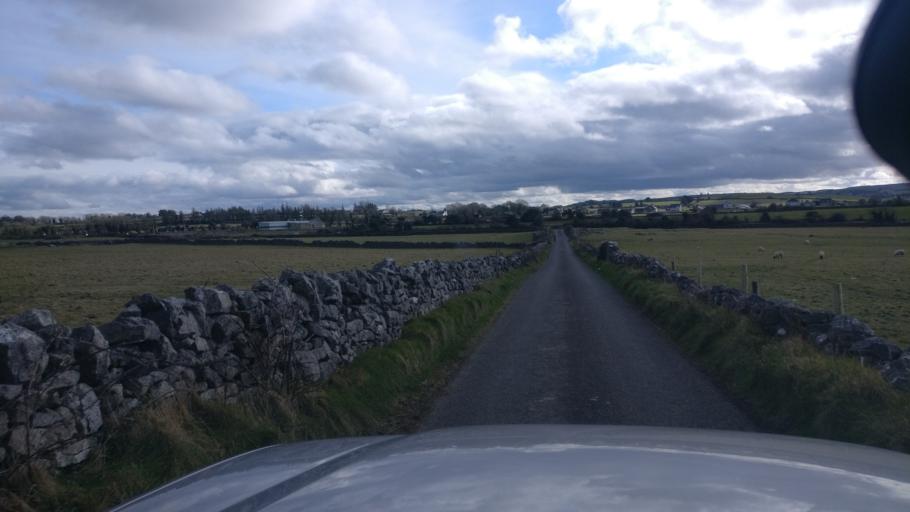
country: IE
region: Connaught
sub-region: County Galway
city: Loughrea
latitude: 53.1990
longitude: -8.5423
